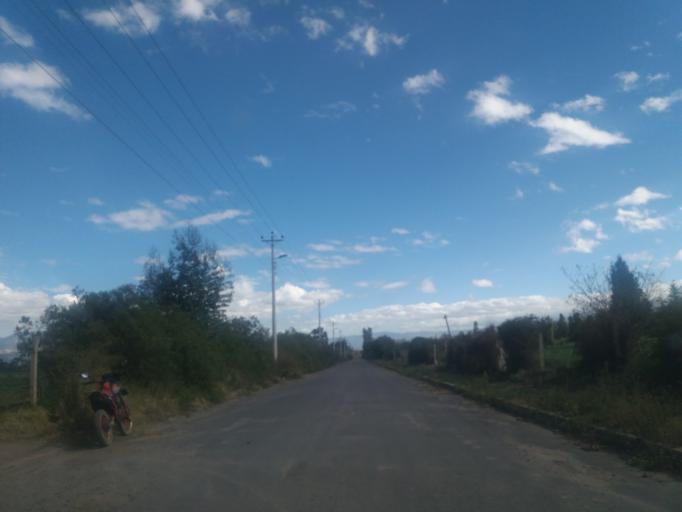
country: EC
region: Pichincha
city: Quito
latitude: -0.1759
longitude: -78.3382
